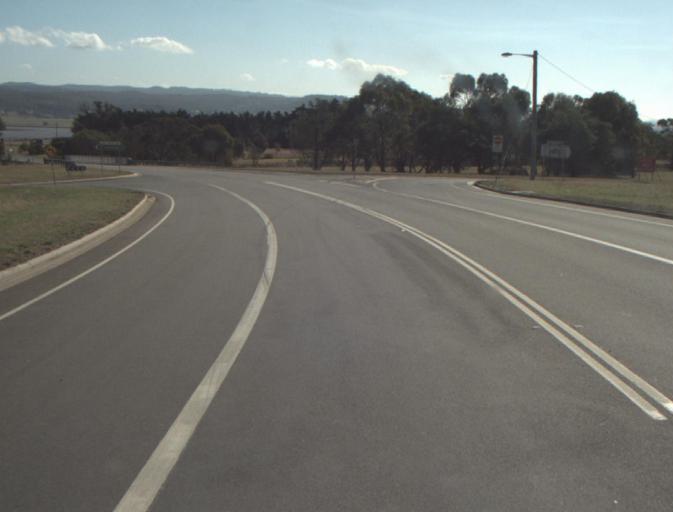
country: AU
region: Tasmania
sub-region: Launceston
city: Mayfield
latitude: -41.3712
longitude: 147.1120
